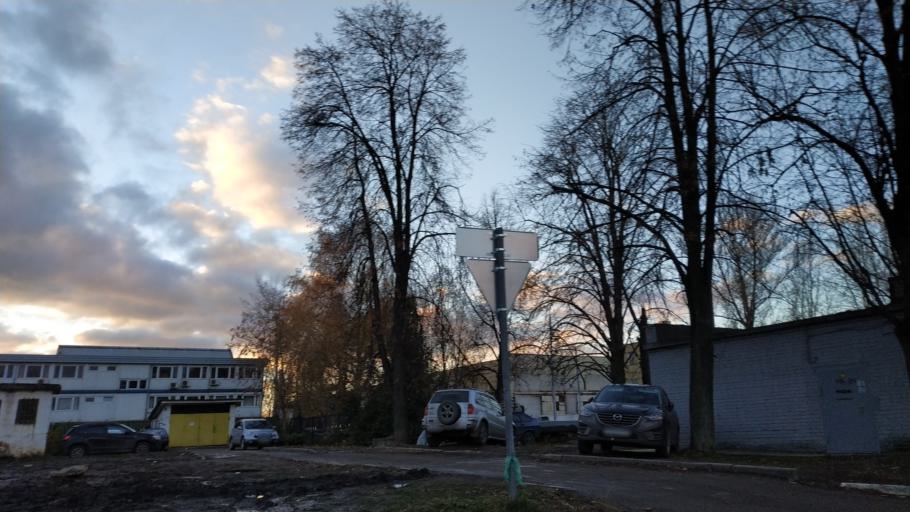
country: RU
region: Moskovskaya
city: Lobnya
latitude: 55.9837
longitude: 37.4153
